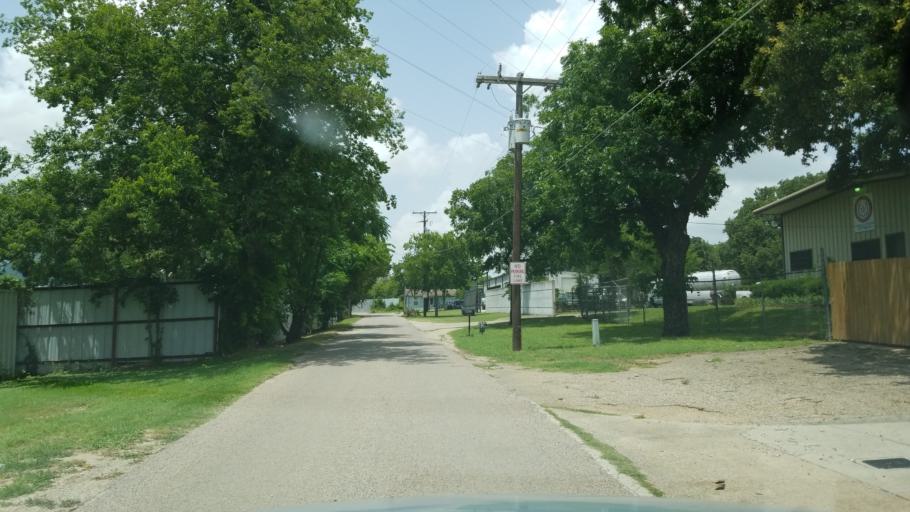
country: US
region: Texas
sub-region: Dallas County
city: Irving
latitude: 32.8273
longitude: -96.9069
